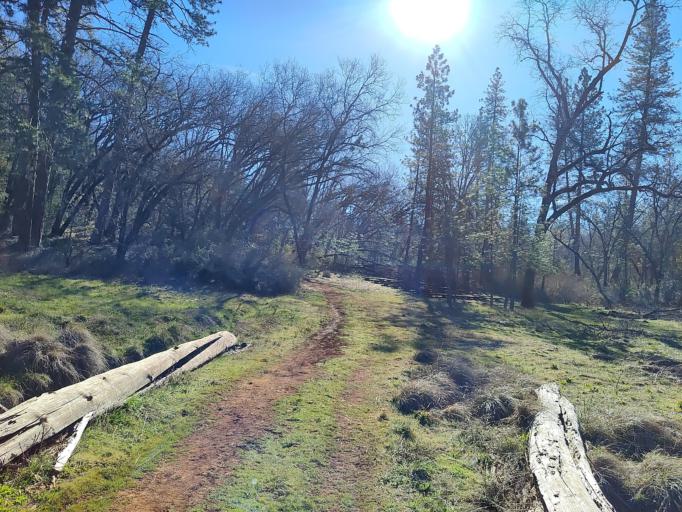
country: US
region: California
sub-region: Placer County
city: Meadow Vista
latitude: 39.0238
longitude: -120.9868
